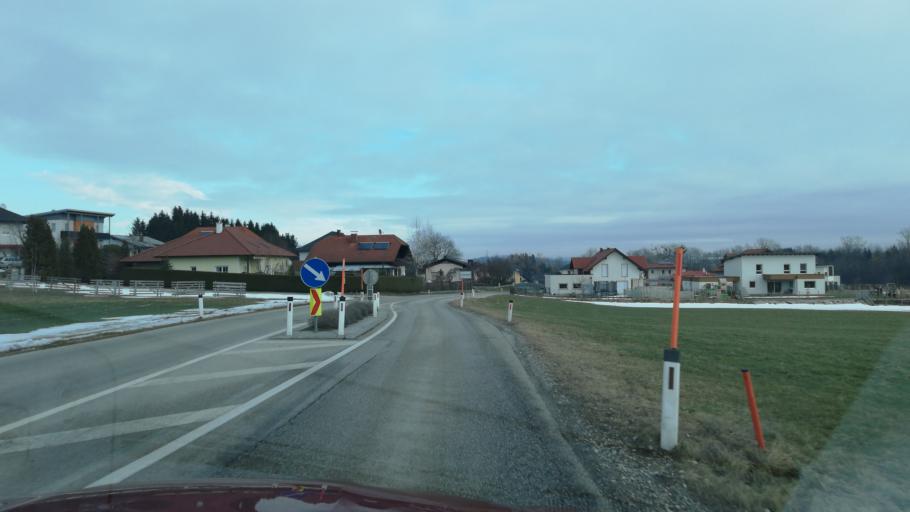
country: AT
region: Upper Austria
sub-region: Politischer Bezirk Vocklabruck
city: Wolfsegg am Hausruck
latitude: 48.1705
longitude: 13.6824
